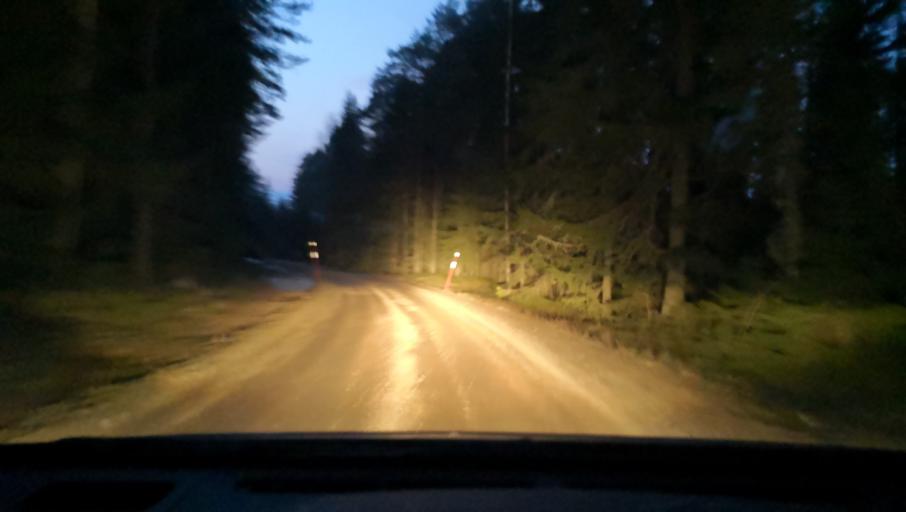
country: SE
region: OErebro
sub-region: Lindesbergs Kommun
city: Frovi
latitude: 59.5891
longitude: 15.4712
